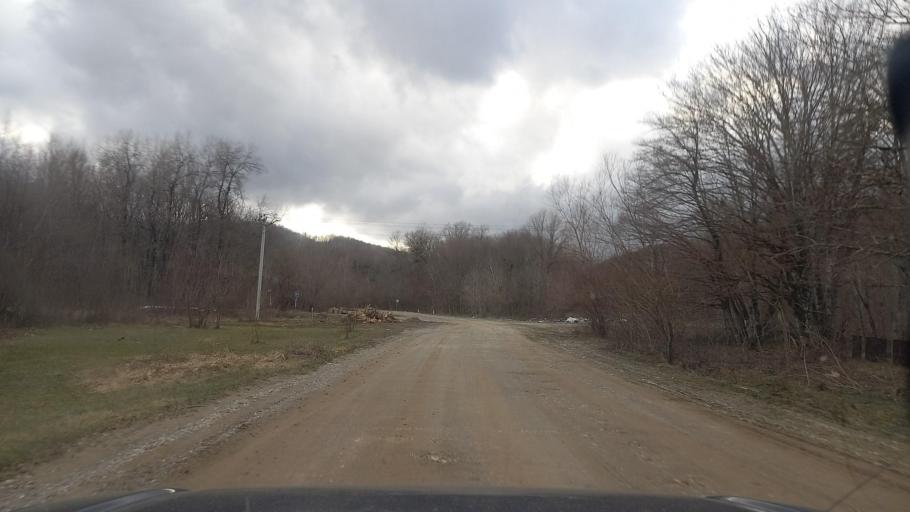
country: RU
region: Krasnodarskiy
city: Smolenskaya
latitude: 44.5603
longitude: 38.7967
